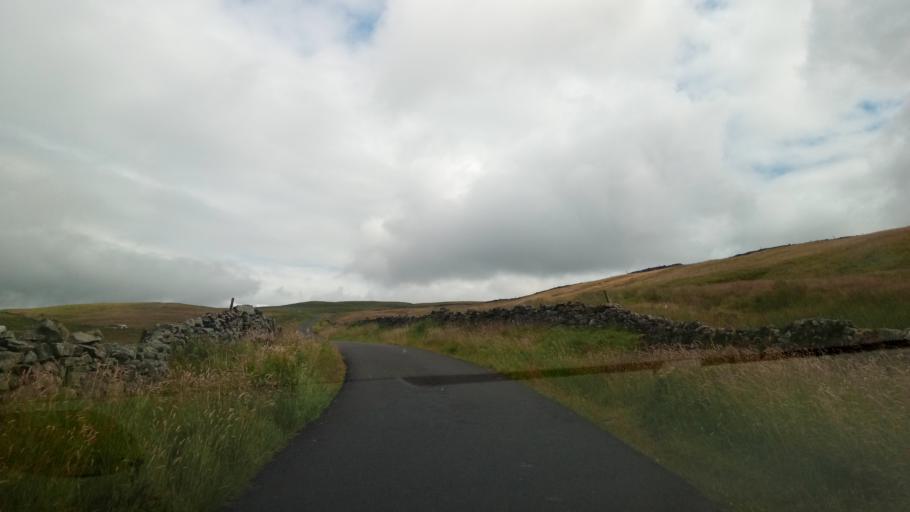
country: GB
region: England
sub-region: North Yorkshire
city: Ingleton
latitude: 54.2866
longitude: -2.3443
